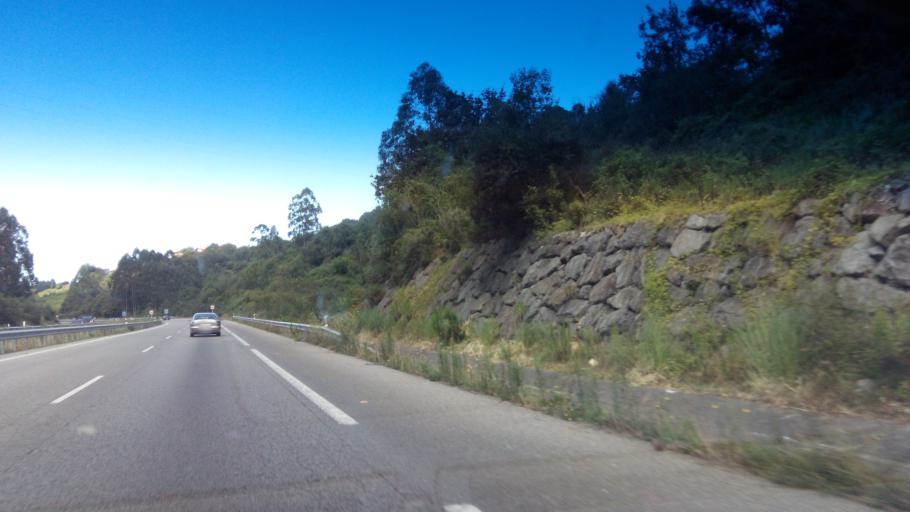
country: ES
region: Asturias
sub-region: Province of Asturias
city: Ribadesella
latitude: 43.4391
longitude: -5.0761
